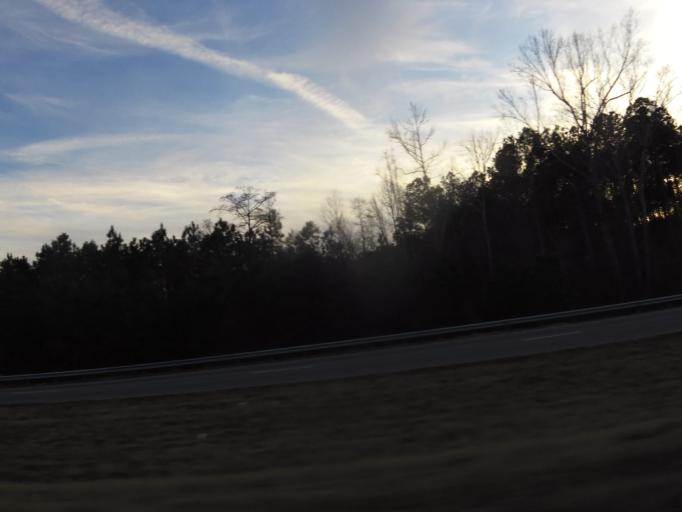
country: US
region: Virginia
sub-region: Southampton County
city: Courtland
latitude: 36.6834
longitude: -77.0157
